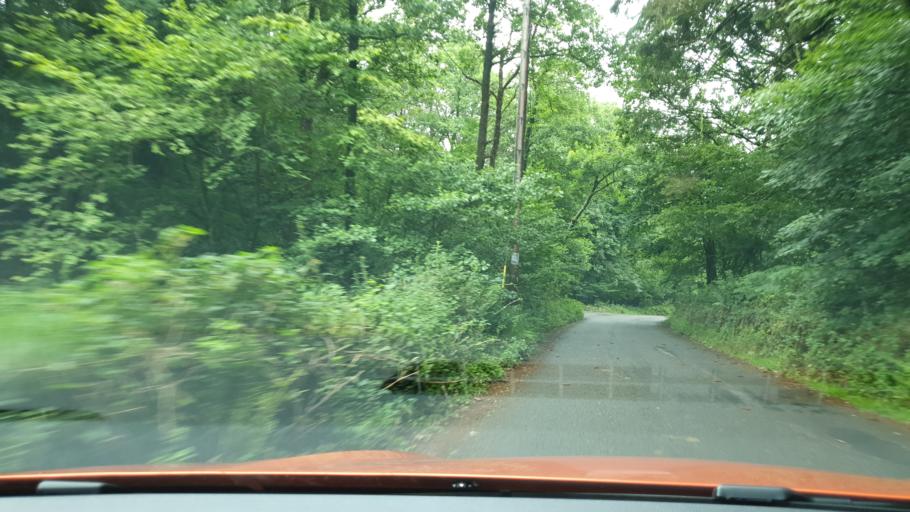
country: GB
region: England
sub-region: Cumbria
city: Grange-over-Sands
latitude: 54.2702
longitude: -2.9867
